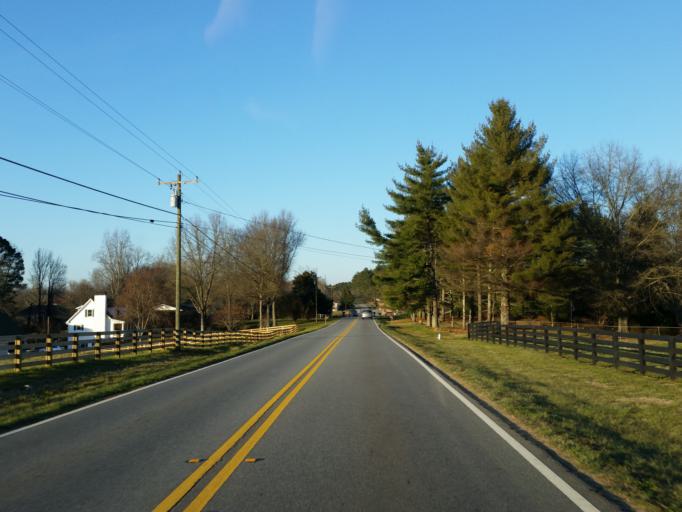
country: US
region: Georgia
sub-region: Cherokee County
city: Holly Springs
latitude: 34.1595
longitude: -84.4277
